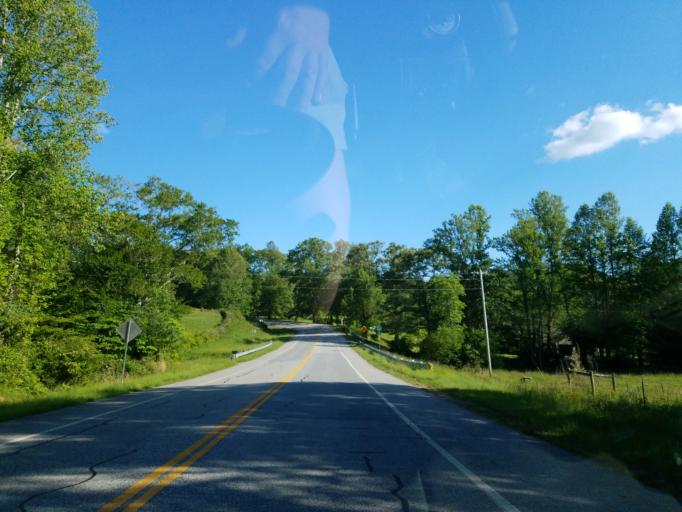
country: US
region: Georgia
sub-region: Fannin County
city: Blue Ridge
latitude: 34.8446
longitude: -84.1949
